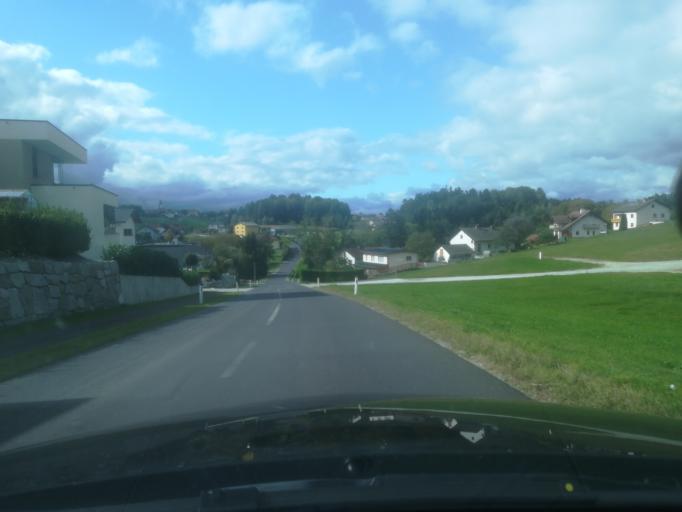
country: AT
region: Upper Austria
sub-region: Politischer Bezirk Urfahr-Umgebung
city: Herzogsdorf
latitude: 48.4291
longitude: 14.1264
